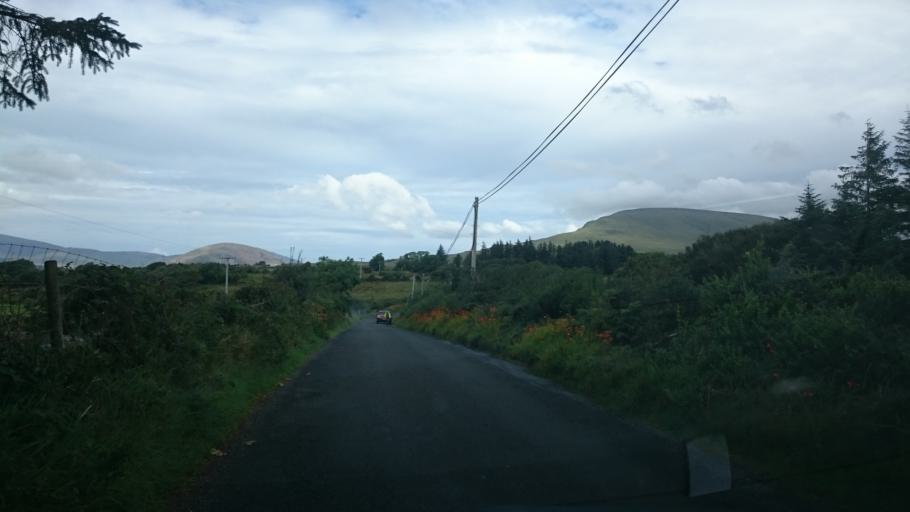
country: IE
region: Connaught
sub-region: Maigh Eo
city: Westport
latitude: 53.9095
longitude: -9.5528
